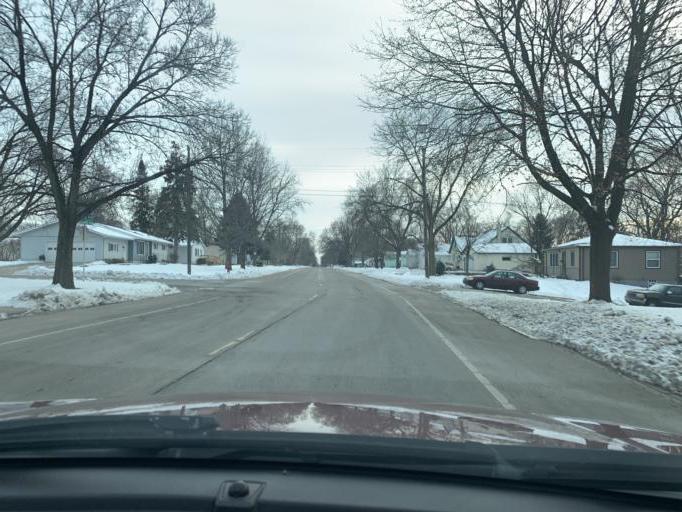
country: US
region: Minnesota
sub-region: Washington County
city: Saint Paul Park
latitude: 44.8407
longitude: -92.9914
